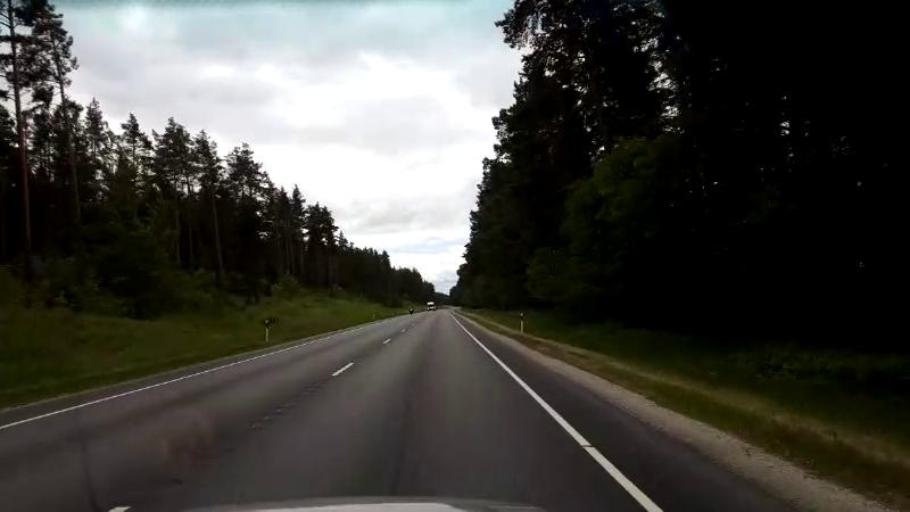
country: EE
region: Paernumaa
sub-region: Paernu linn
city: Parnu
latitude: 58.1690
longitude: 24.4958
